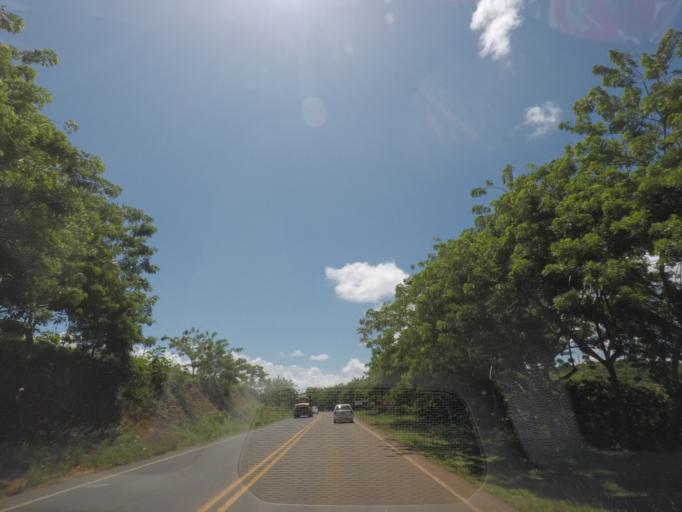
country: BR
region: Bahia
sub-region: Valenca
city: Valenca
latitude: -13.3355
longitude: -39.0616
